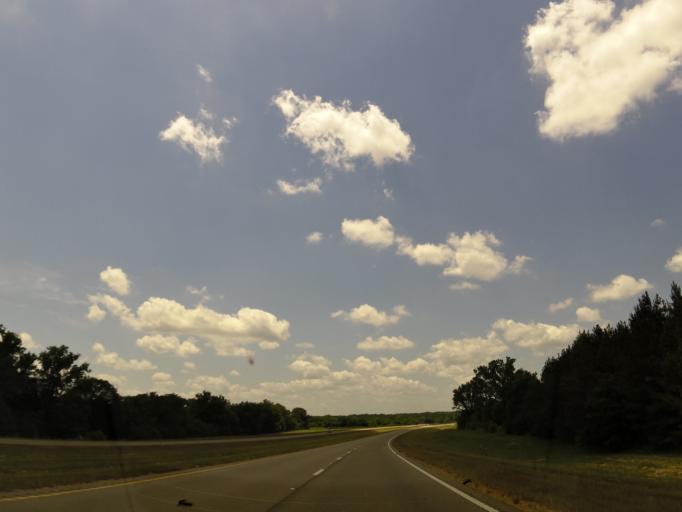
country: US
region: Mississippi
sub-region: Pontotoc County
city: Pontotoc
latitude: 34.2212
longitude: -88.8676
